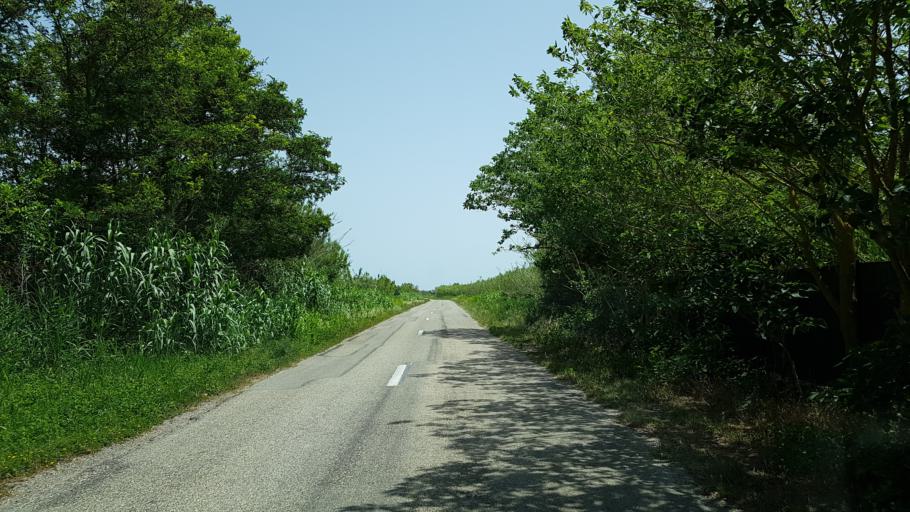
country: FR
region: Provence-Alpes-Cote d'Azur
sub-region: Departement des Bouches-du-Rhone
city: Port-Saint-Louis-du-Rhone
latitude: 43.4418
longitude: 4.6781
